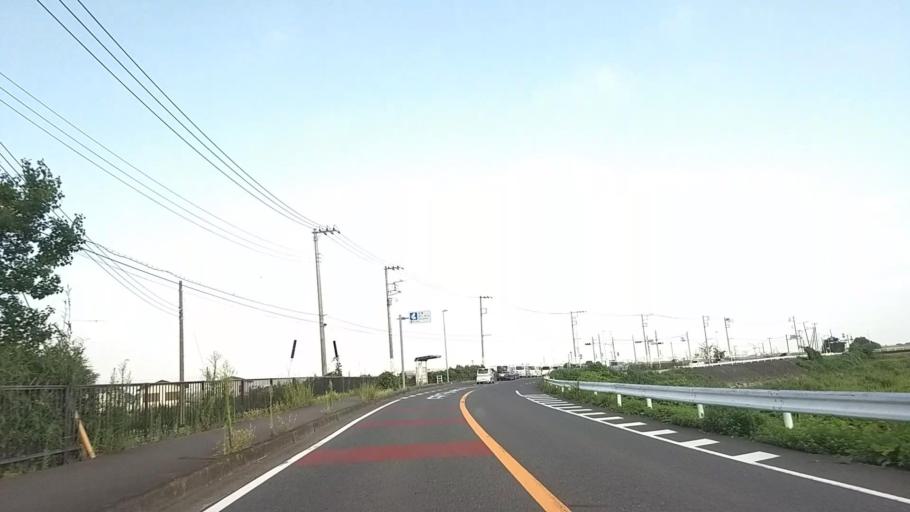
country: JP
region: Kanagawa
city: Isehara
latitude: 35.3562
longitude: 139.3079
